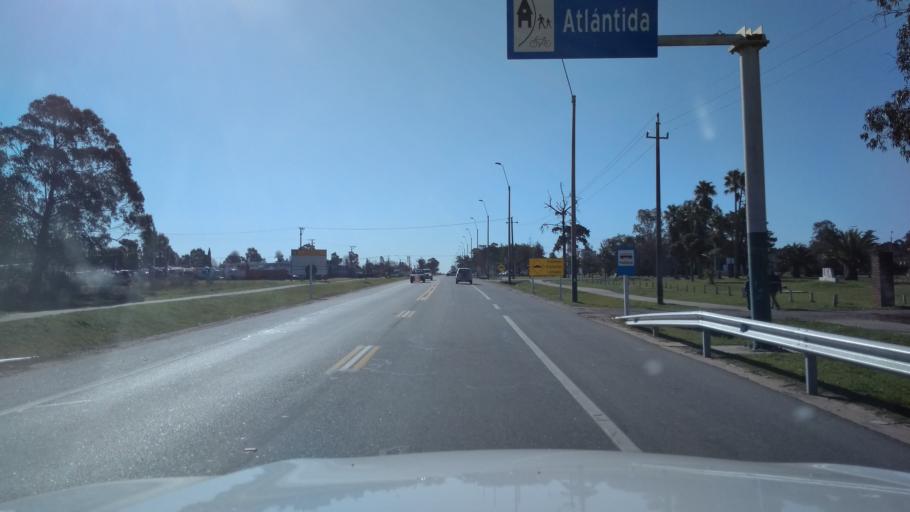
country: UY
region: Canelones
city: Atlantida
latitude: -34.7632
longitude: -55.7650
